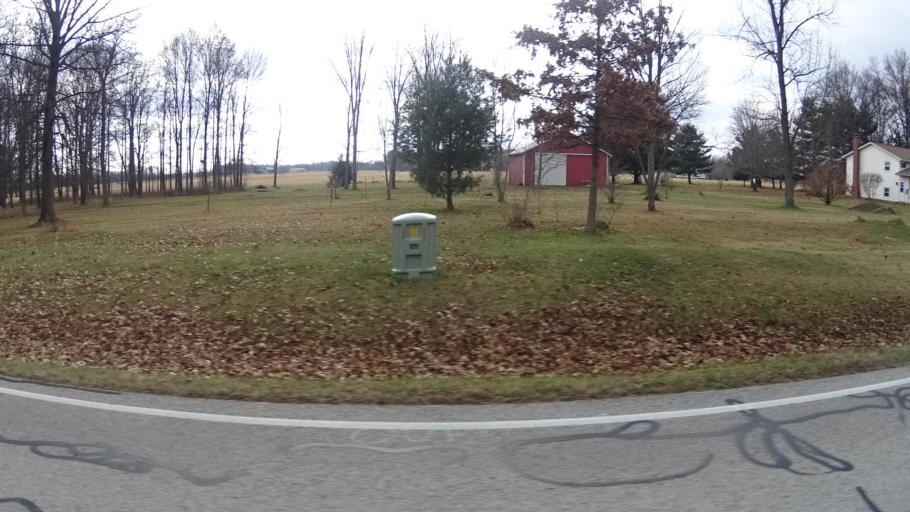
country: US
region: Ohio
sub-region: Lorain County
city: Oberlin
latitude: 41.2827
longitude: -82.1933
